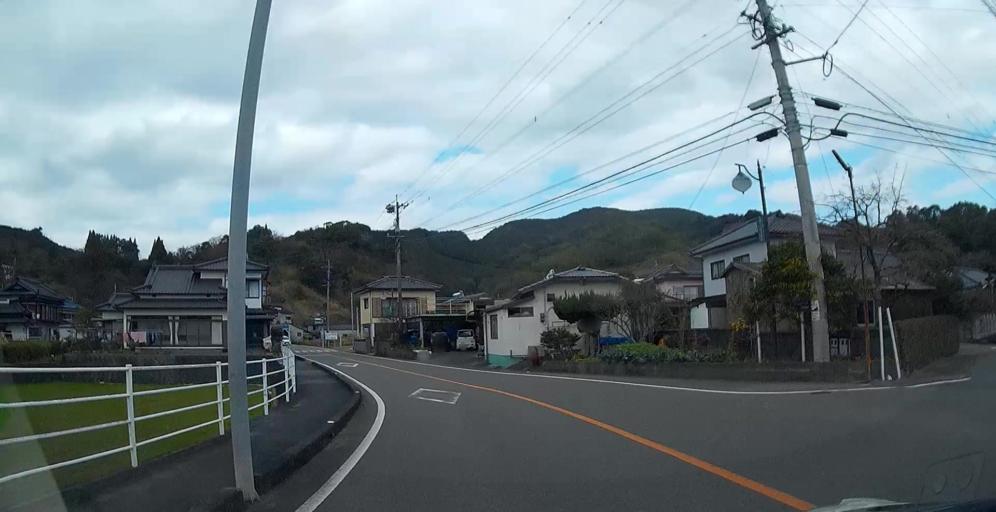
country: JP
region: Kumamoto
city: Yatsushiro
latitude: 32.3649
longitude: 130.5097
